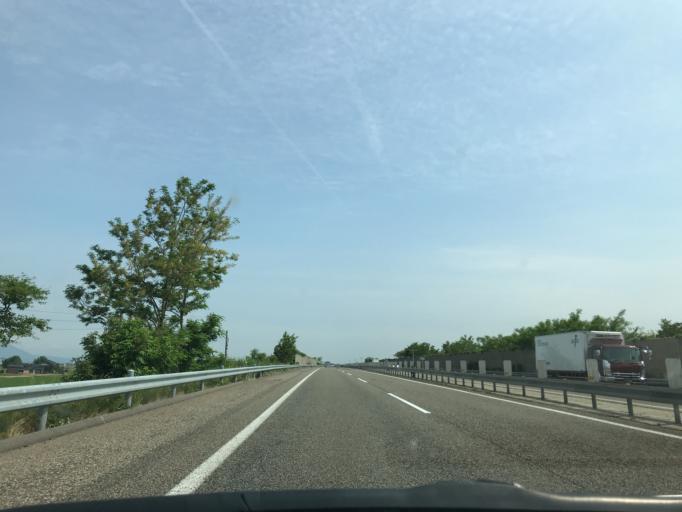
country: JP
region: Niigata
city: Mitsuke
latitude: 37.5760
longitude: 138.8885
